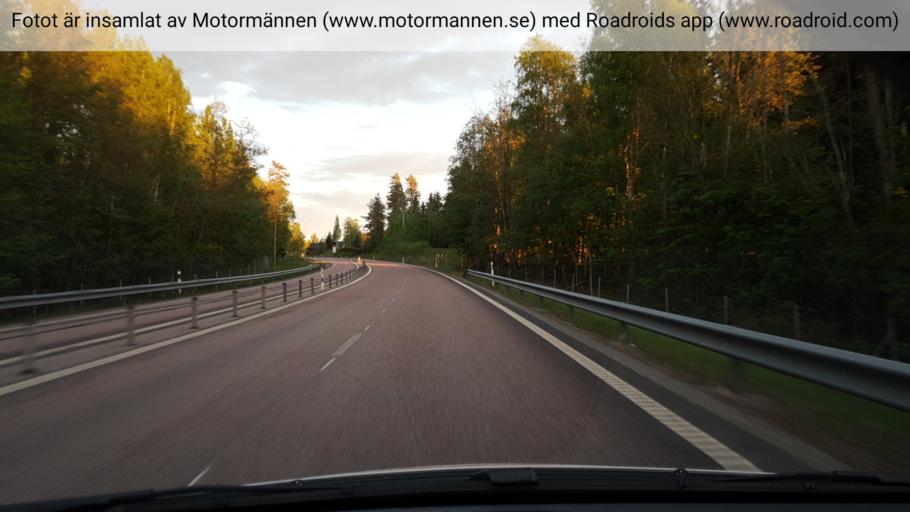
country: SE
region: Vaestmanland
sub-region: Fagersta Kommun
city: Fagersta
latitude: 59.9535
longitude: 15.8470
